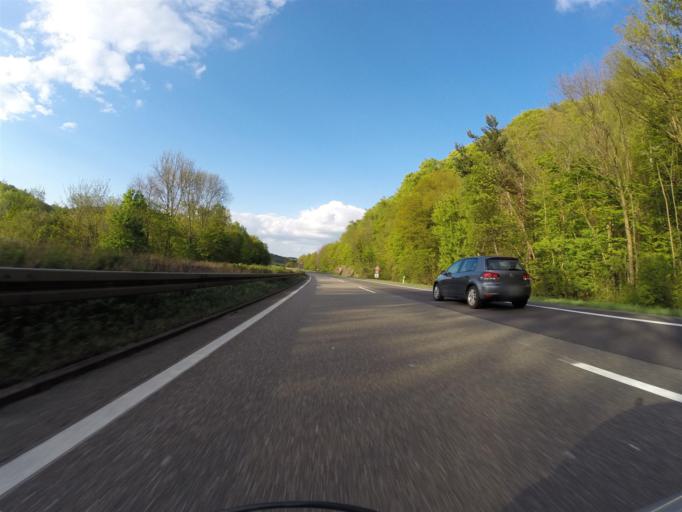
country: DE
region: Saarland
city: Sankt Ingbert
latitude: 49.2420
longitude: 7.0870
